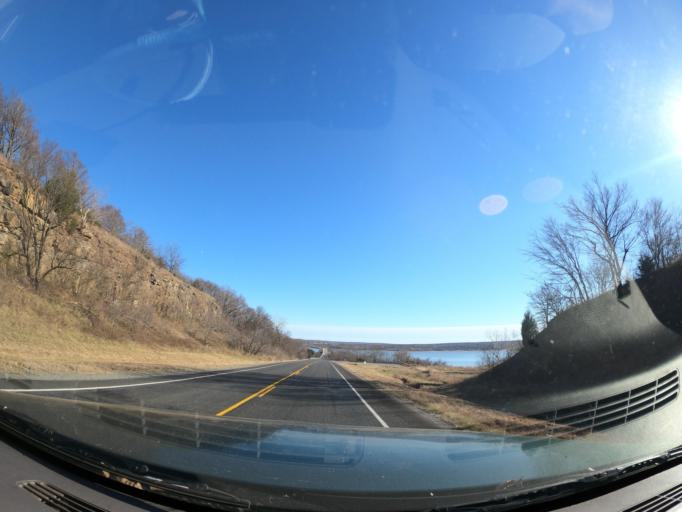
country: US
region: Oklahoma
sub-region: McIntosh County
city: Eufaula
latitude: 35.2512
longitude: -95.5720
